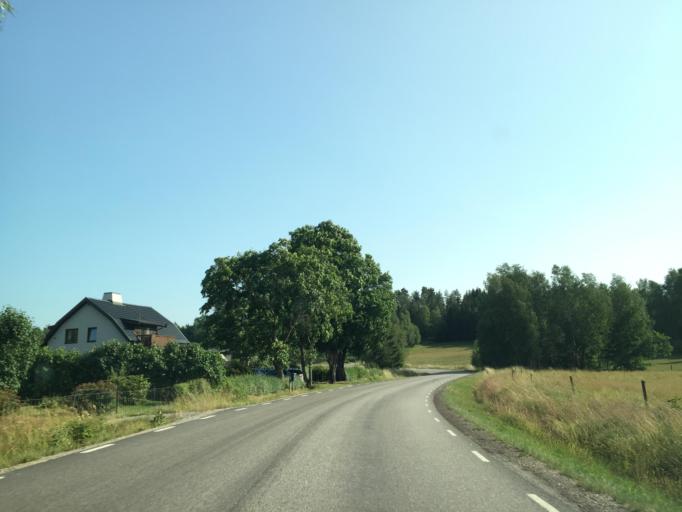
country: SE
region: Vaestra Goetaland
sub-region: Trollhattan
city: Trollhattan
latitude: 58.2749
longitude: 12.2482
